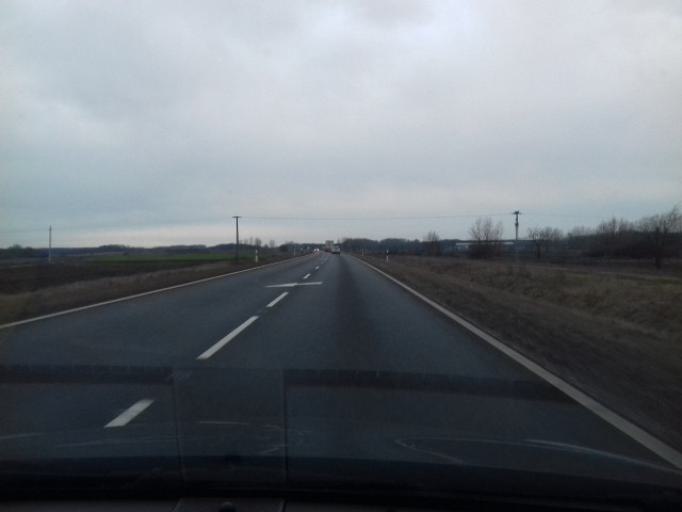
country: HU
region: Szabolcs-Szatmar-Bereg
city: Nyirpazony
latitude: 47.9409
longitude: 21.8186
